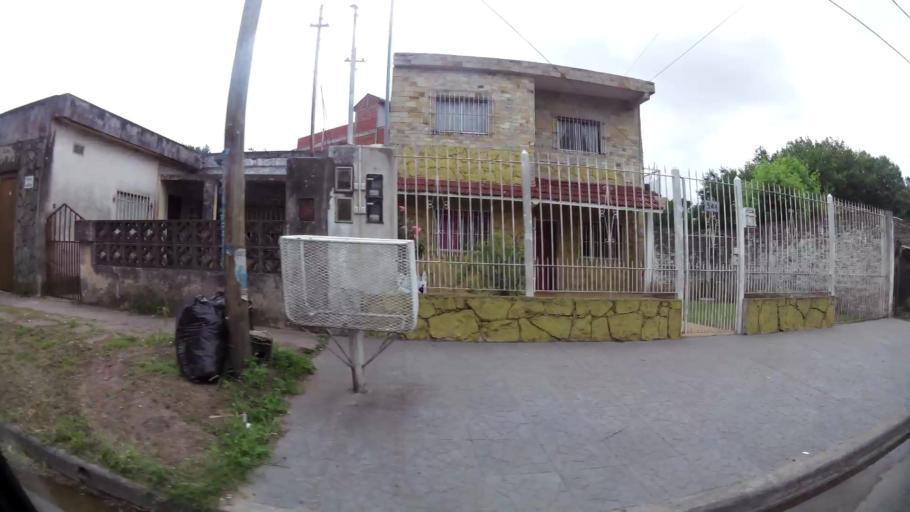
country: AR
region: Buenos Aires
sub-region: Partido de Ezeiza
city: Ezeiza
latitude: -34.8479
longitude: -58.5201
